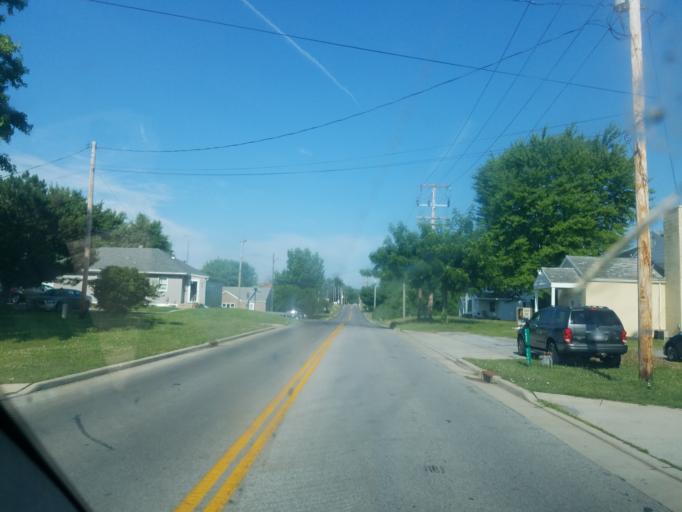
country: US
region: Ohio
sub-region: Allen County
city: Lima
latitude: 40.7423
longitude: -84.0778
